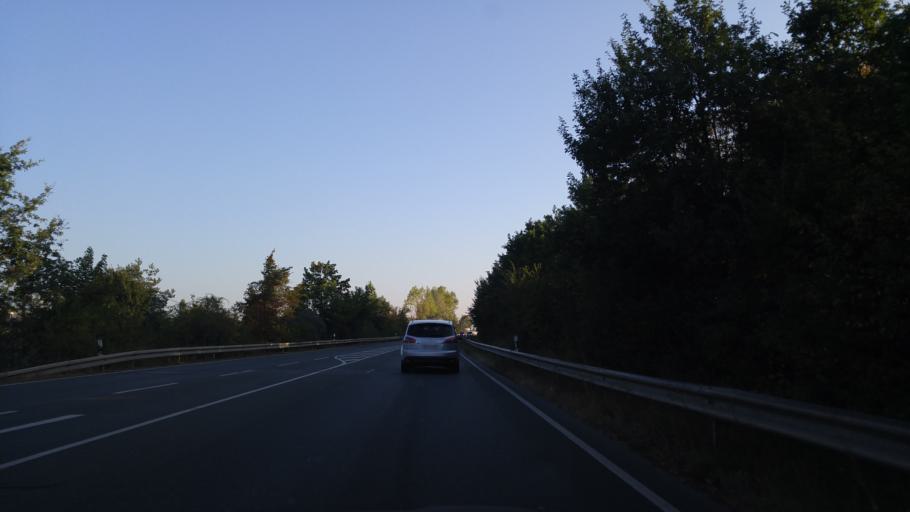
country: DE
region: Bavaria
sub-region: Regierungsbezirk Mittelfranken
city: Zirndorf
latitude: 49.4867
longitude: 10.9431
